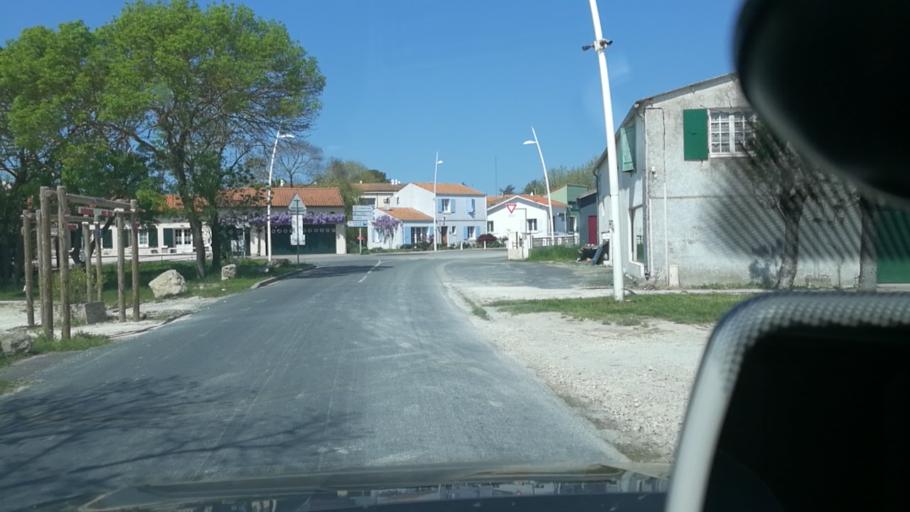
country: FR
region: Poitou-Charentes
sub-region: Departement de la Charente-Maritime
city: Saint-Trojan-les-Bains
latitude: 45.8834
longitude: -1.1958
